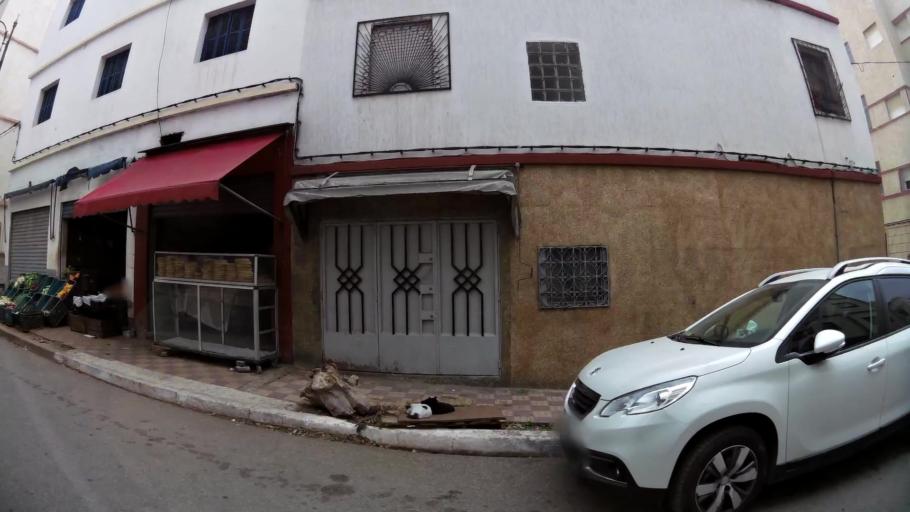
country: MA
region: Tanger-Tetouan
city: Tetouan
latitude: 35.5639
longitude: -5.3673
